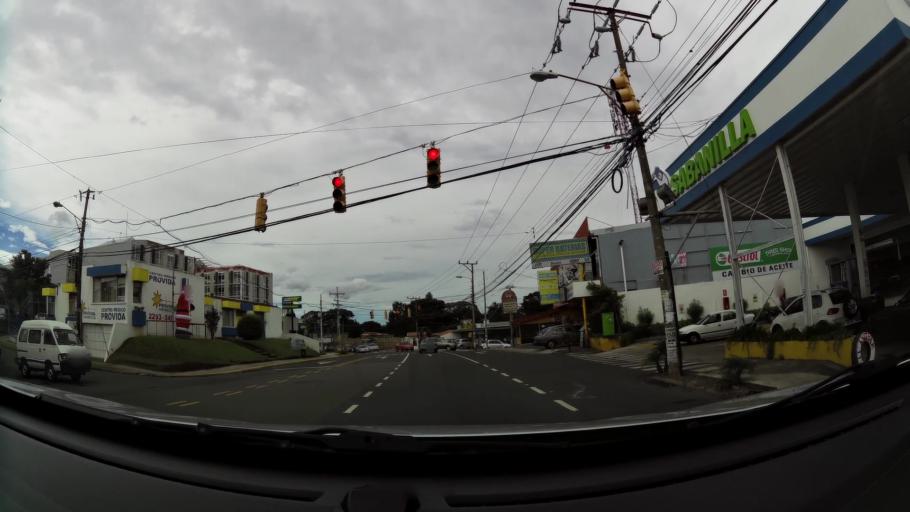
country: CR
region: San Jose
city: Sabanilla
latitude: 9.9432
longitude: -84.0413
